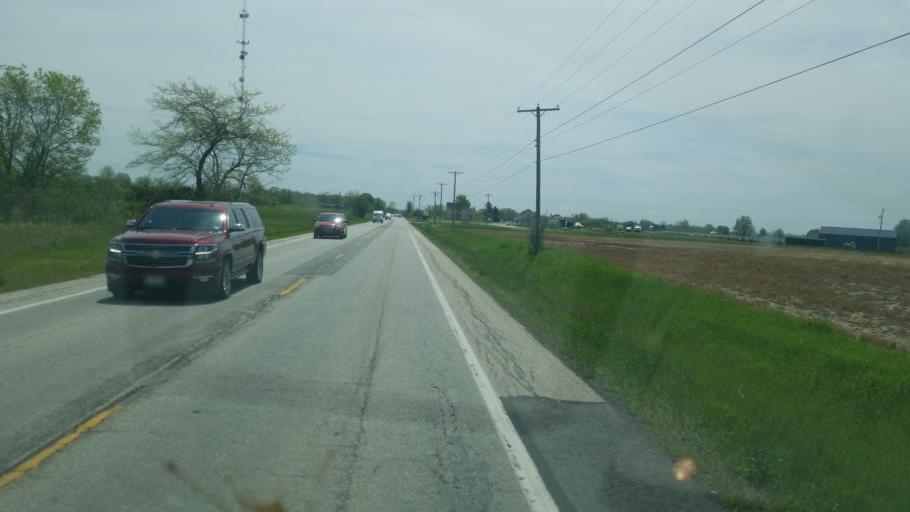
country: US
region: Ohio
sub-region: Ottawa County
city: Oak Harbor
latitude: 41.5795
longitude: -83.0913
